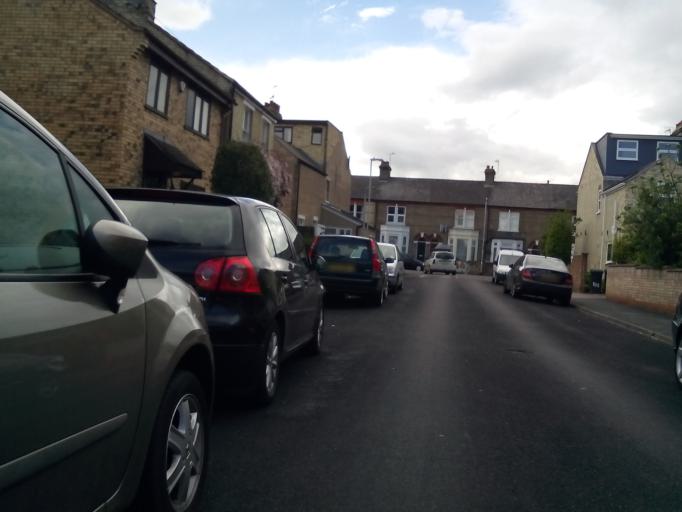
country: GB
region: England
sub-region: Cambridgeshire
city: Cambridge
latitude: 52.1994
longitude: 0.1505
